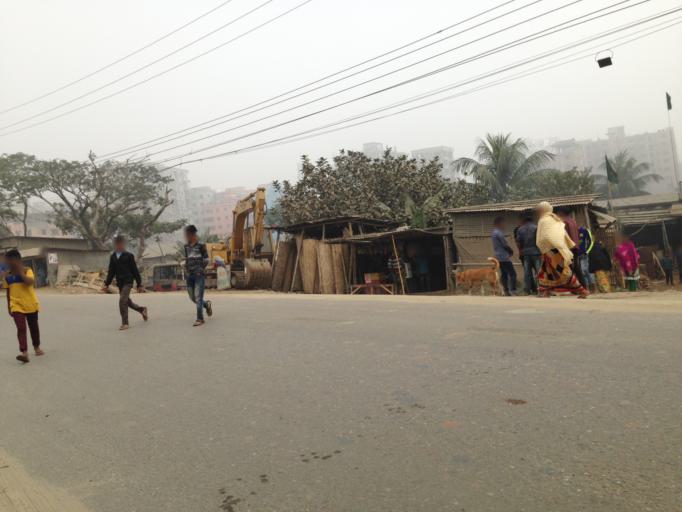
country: BD
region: Dhaka
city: Azimpur
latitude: 23.7999
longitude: 90.3439
